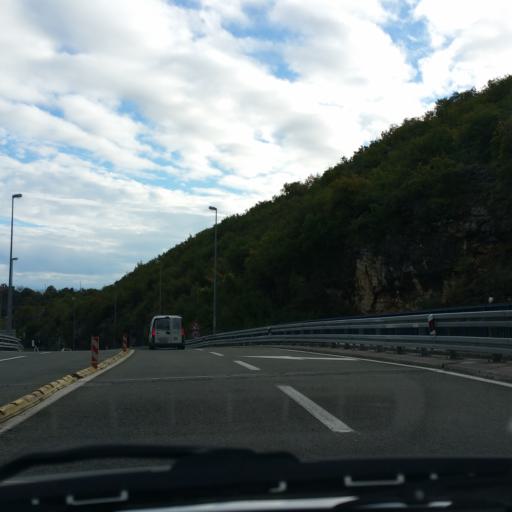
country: HR
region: Primorsko-Goranska
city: Drenova
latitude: 45.3454
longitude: 14.4203
